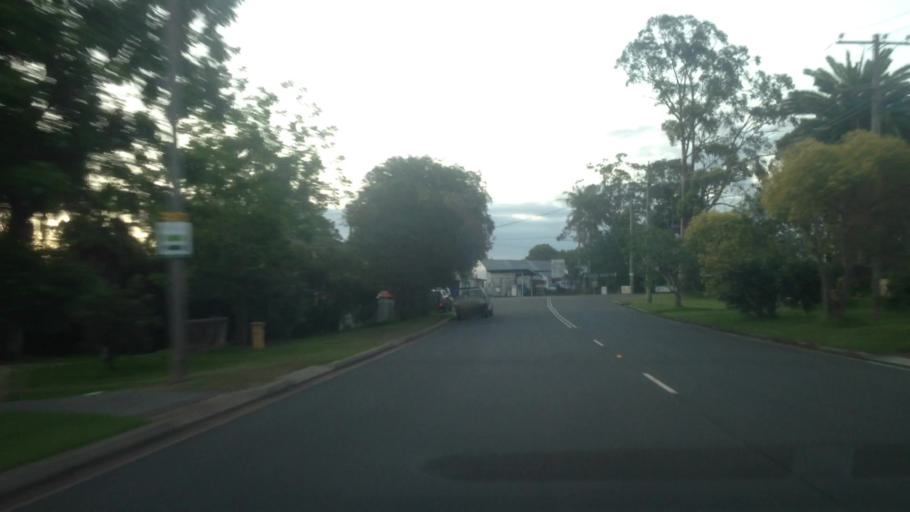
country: AU
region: New South Wales
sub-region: Lake Macquarie Shire
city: Cooranbong
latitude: -33.0703
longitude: 151.4649
